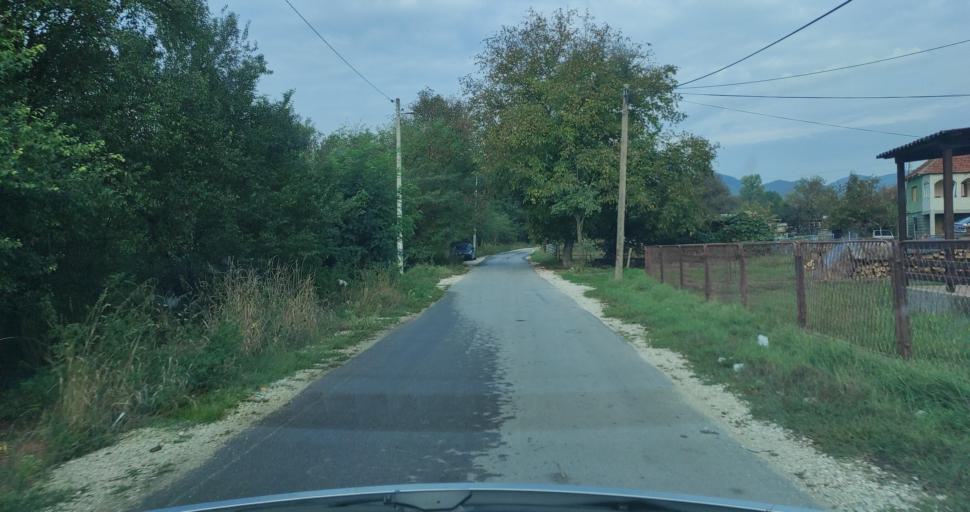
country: RS
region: Central Serbia
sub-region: Pcinjski Okrug
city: Vladicin Han
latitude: 42.6701
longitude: 22.0284
